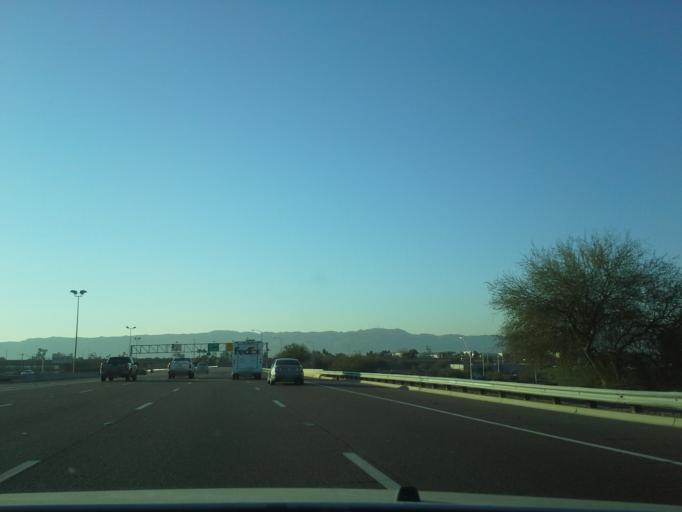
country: US
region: Arizona
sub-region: Maricopa County
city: Phoenix
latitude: 33.4322
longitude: -112.0379
